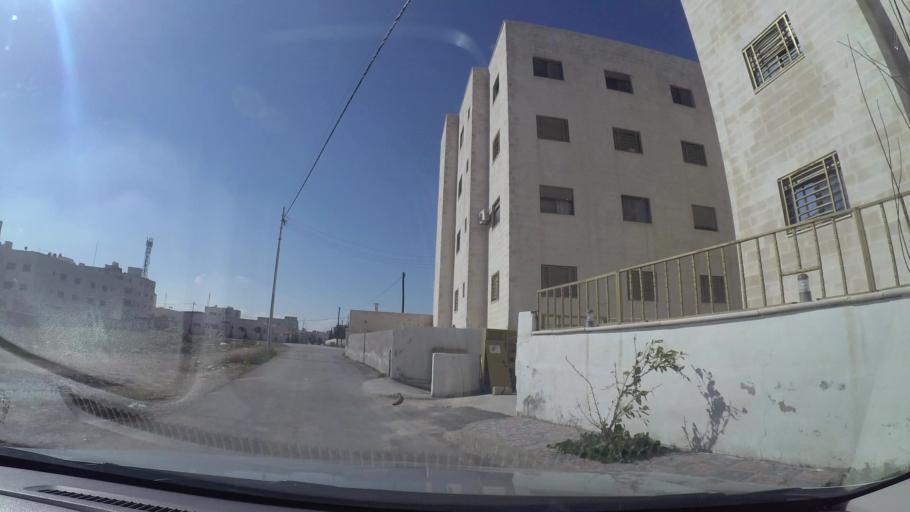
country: JO
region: Amman
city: Al Bunayyat ash Shamaliyah
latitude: 31.9043
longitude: 35.8958
